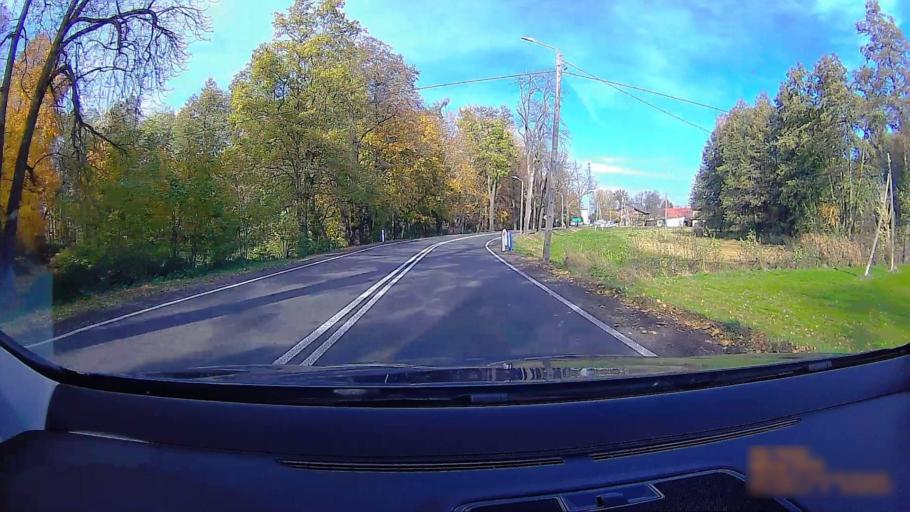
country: PL
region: Greater Poland Voivodeship
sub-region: Powiat ostrzeszowski
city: Doruchow
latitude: 51.4141
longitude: 18.0759
